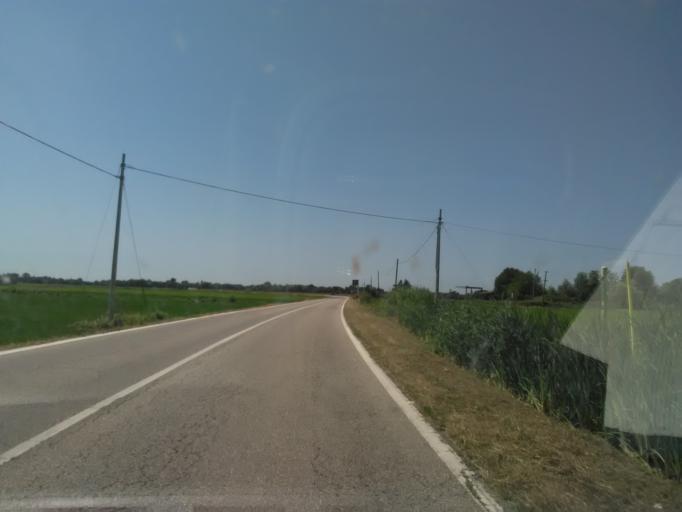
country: IT
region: Piedmont
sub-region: Provincia di Vercelli
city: Oldenico
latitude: 45.3924
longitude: 8.3787
